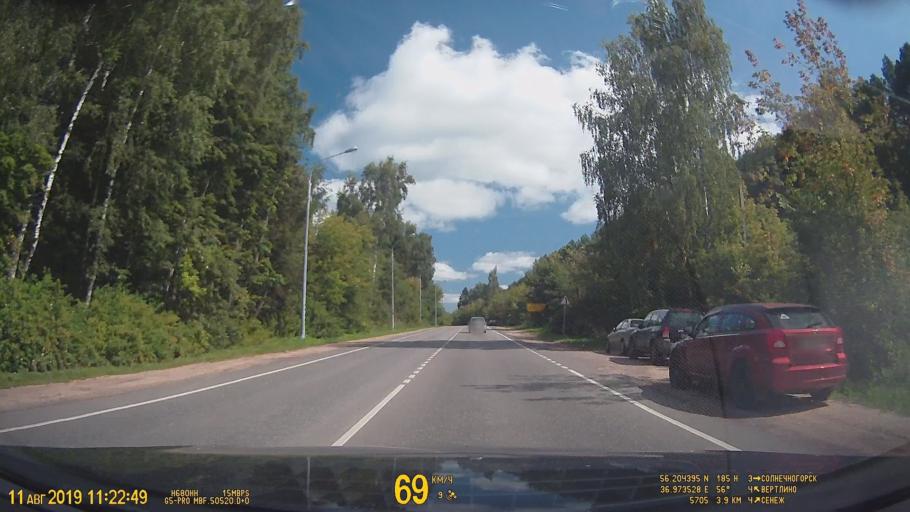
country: RU
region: Moskovskaya
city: Solnechnogorsk
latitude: 56.2046
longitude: 36.9740
